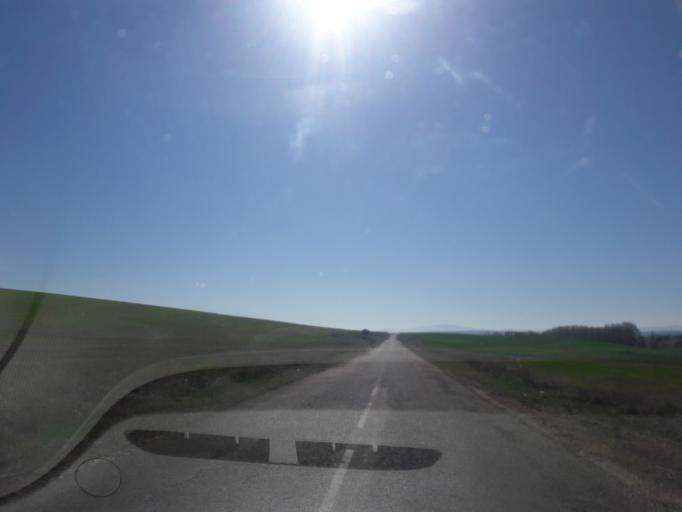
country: ES
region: Castille and Leon
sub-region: Provincia de Salamanca
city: Mancera de Abajo
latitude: 40.8274
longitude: -5.1830
